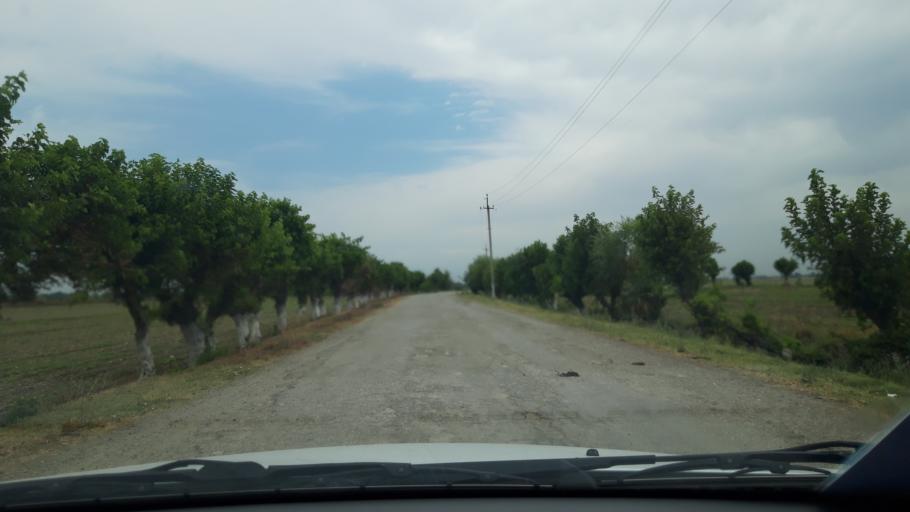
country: UZ
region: Namangan
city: Uychi
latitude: 41.0189
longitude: 71.9215
